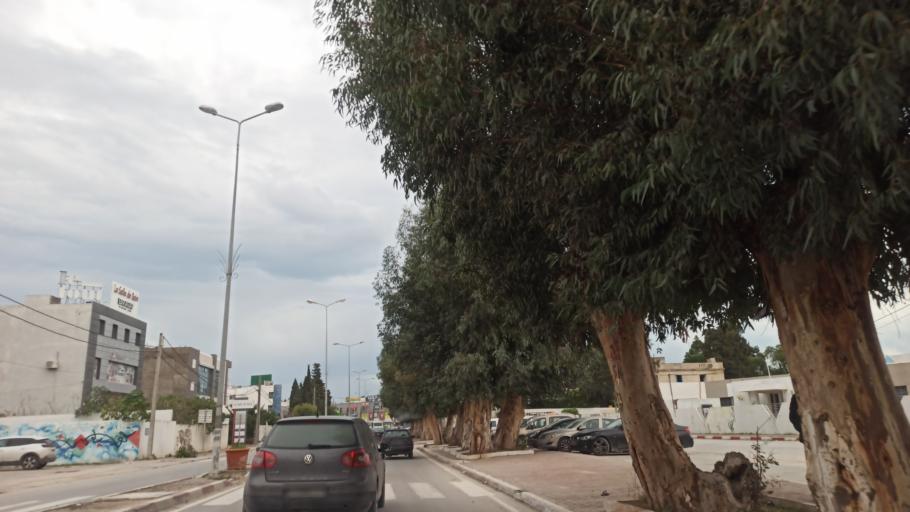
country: TN
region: Ariana
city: Ariana
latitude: 36.8748
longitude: 10.2423
